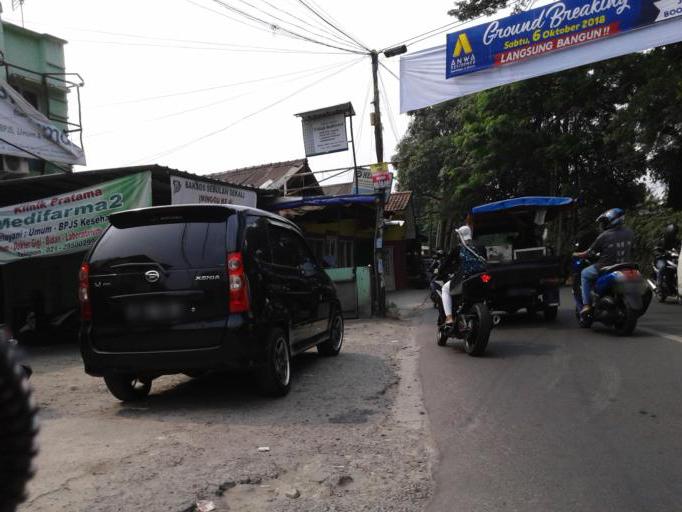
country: ID
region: Banten
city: South Tangerang
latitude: -6.2926
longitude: 106.7327
